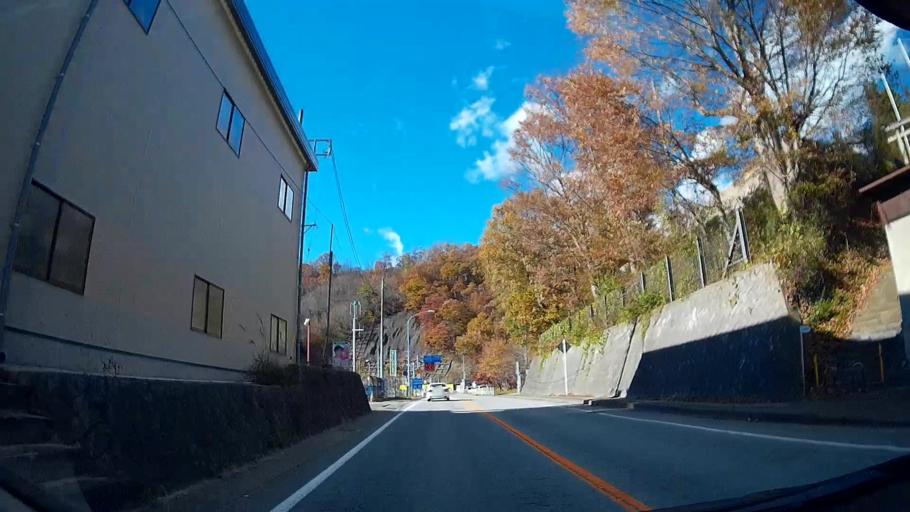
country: JP
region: Yamanashi
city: Otsuki
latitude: 35.6017
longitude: 138.9030
